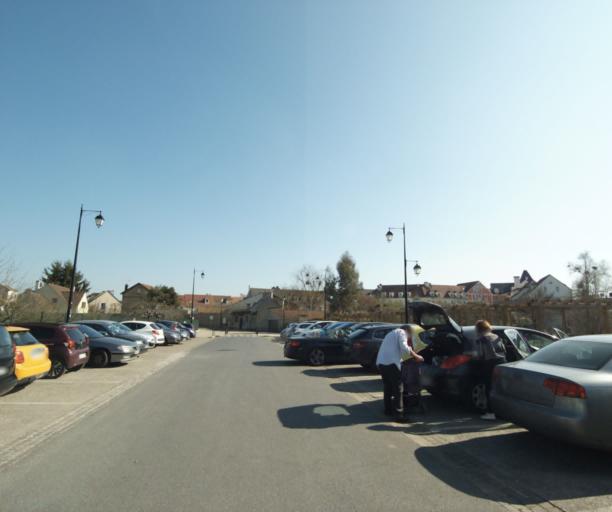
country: FR
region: Ile-de-France
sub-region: Departement du Val-d'Oise
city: Cergy
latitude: 49.0328
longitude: 2.0595
